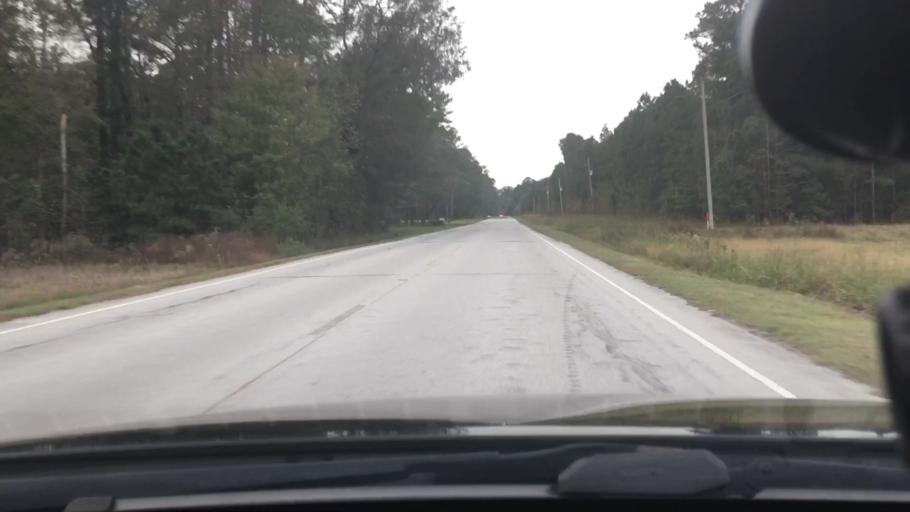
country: US
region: North Carolina
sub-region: Craven County
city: Vanceboro
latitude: 35.4035
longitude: -77.2403
